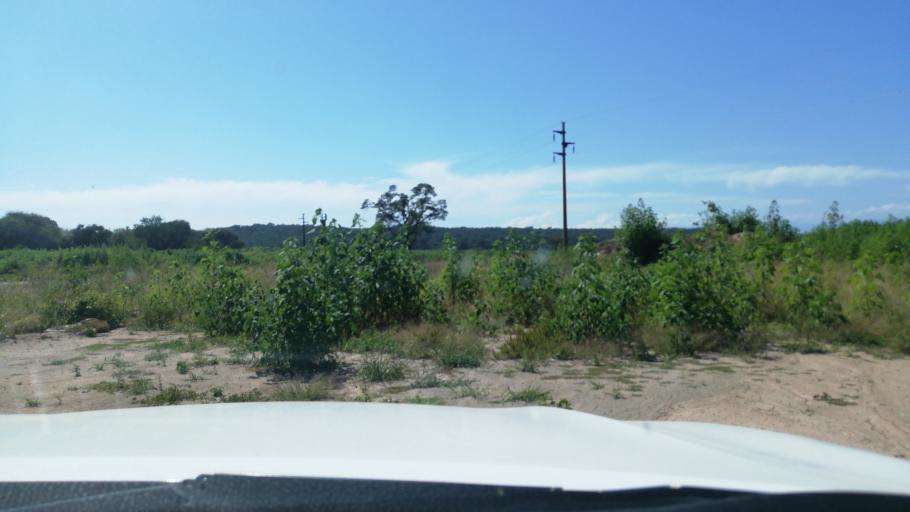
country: AR
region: Jujuy
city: La Mendieta
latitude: -24.3754
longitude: -65.0014
